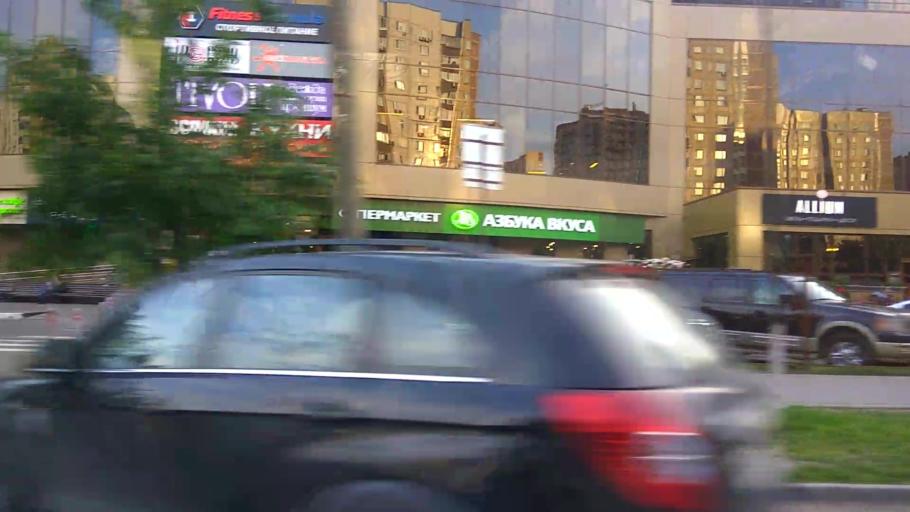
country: RU
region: Moskovskaya
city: Yubileyny
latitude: 55.9206
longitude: 37.8683
